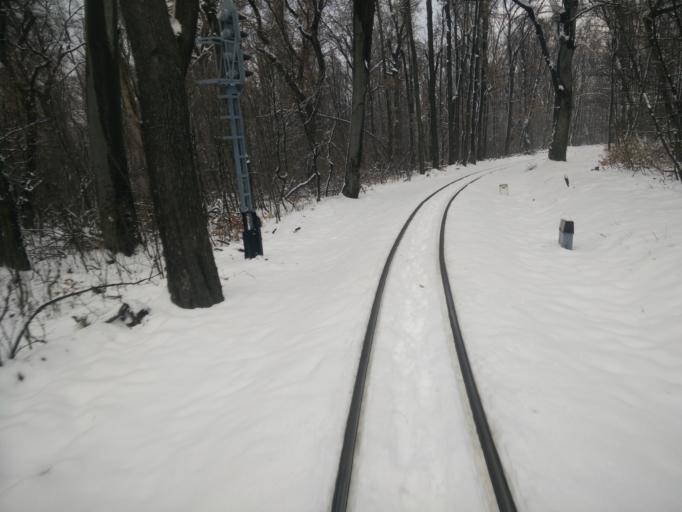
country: HU
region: Pest
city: Budakeszi
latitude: 47.4992
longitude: 18.9584
